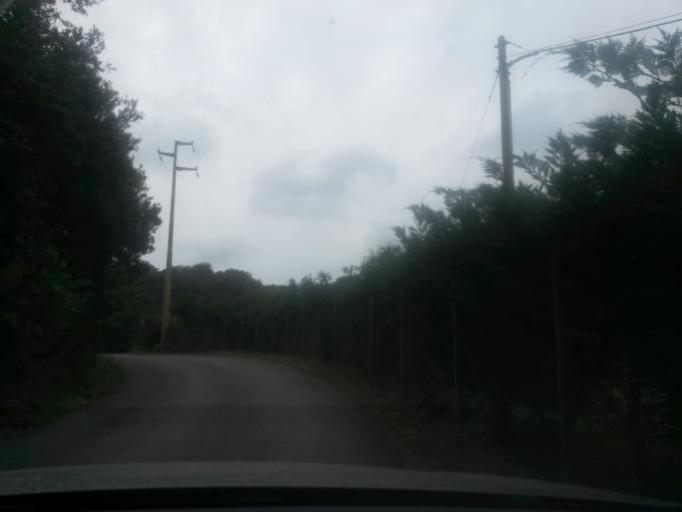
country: IT
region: Tuscany
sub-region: Provincia di Livorno
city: Porto Azzurro
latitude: 42.7439
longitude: 10.4074
